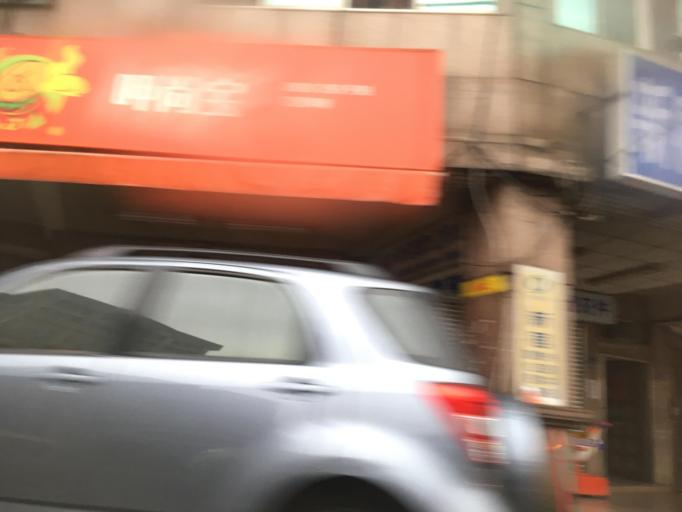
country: TW
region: Taiwan
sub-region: Keelung
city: Keelung
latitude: 25.1000
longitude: 121.7363
